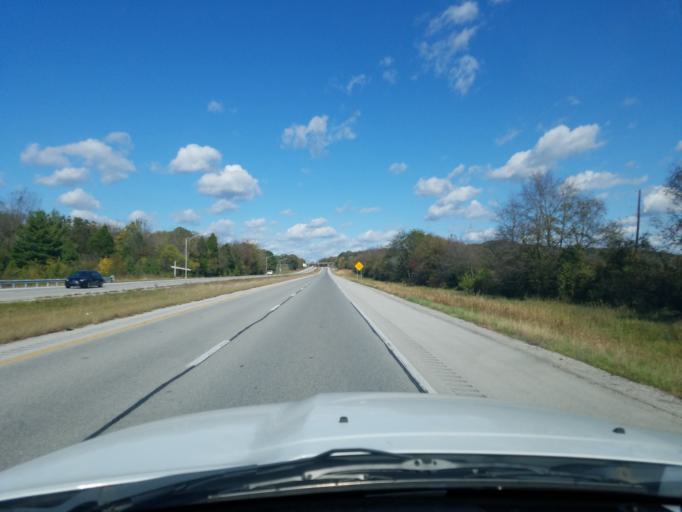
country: US
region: Kentucky
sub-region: Warren County
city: Bowling Green
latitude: 36.9938
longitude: -86.5044
